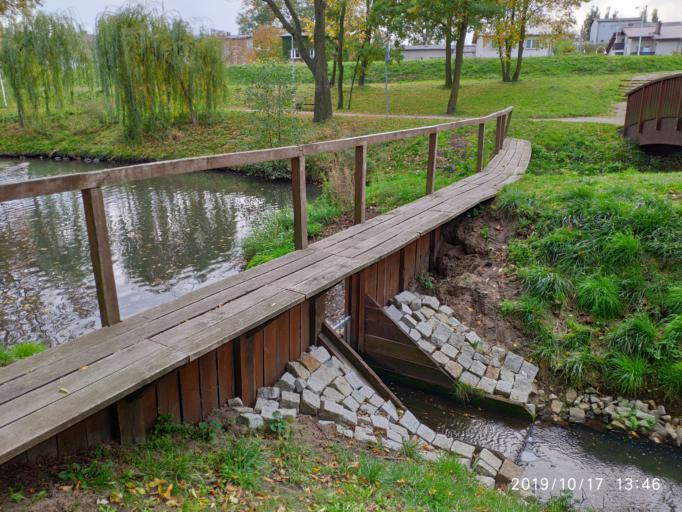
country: PL
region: Lubusz
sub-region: Zielona Gora
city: Zielona Gora
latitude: 51.9498
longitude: 15.5269
